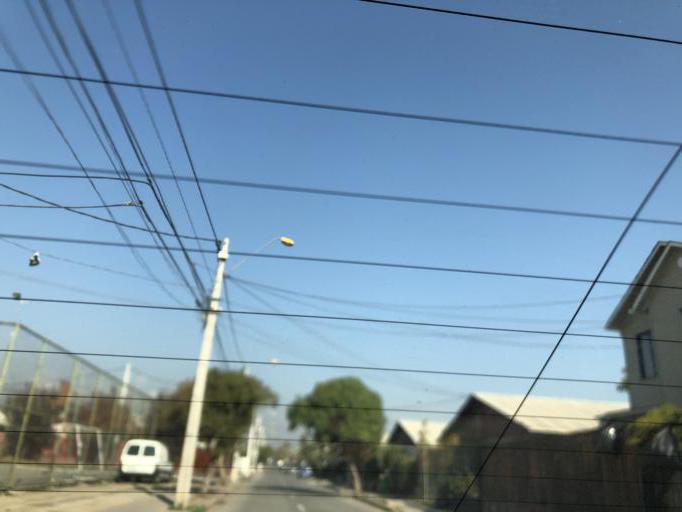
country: CL
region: Santiago Metropolitan
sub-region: Provincia de Cordillera
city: Puente Alto
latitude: -33.6138
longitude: -70.5586
